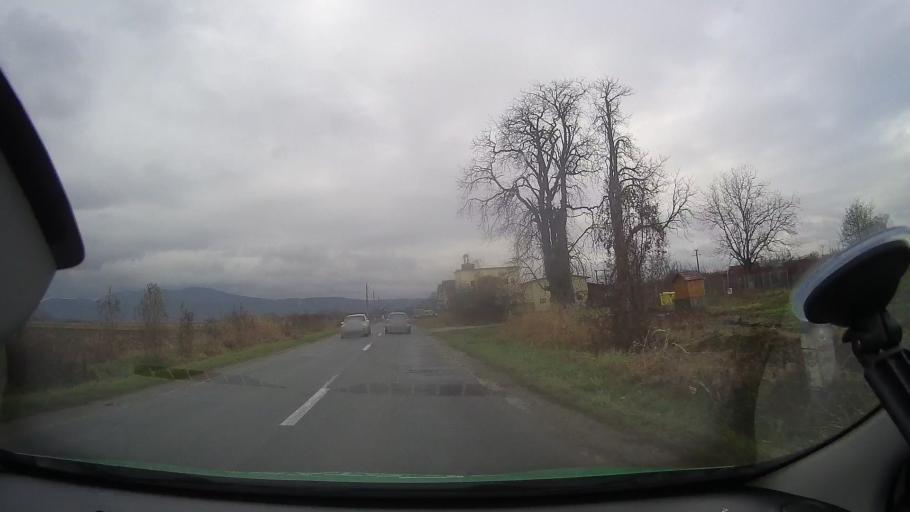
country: RO
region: Arad
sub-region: Comuna Buteni
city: Buteni
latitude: 46.3365
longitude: 22.1269
